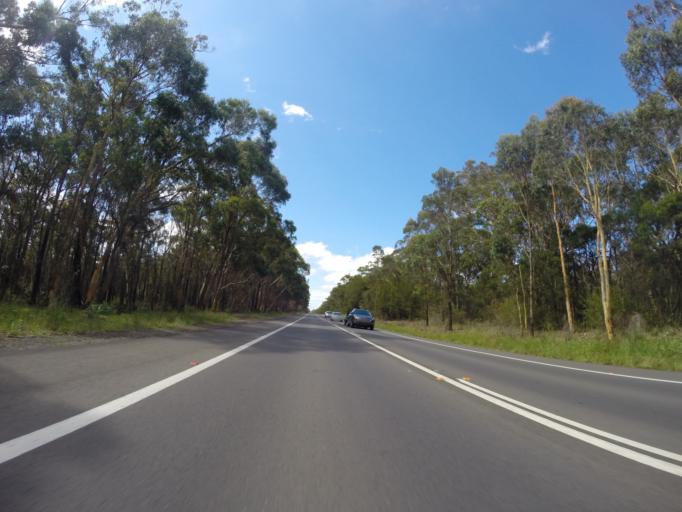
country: AU
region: New South Wales
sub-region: Shoalhaven Shire
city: Falls Creek
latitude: -35.0107
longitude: 150.5813
